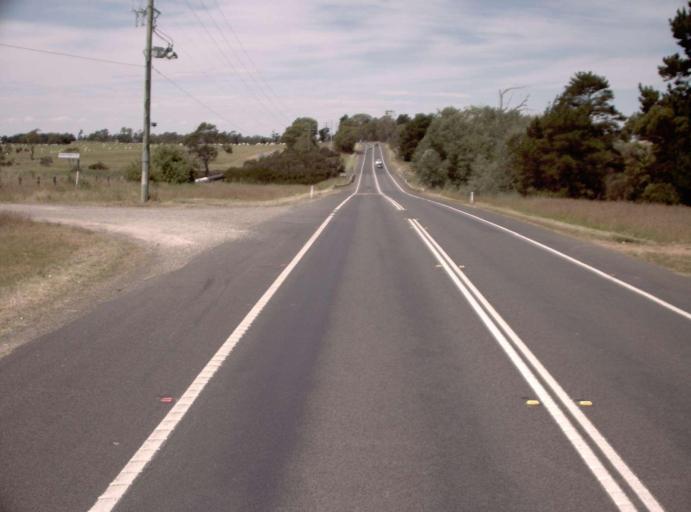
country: AU
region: Victoria
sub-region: Latrobe
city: Traralgon
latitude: -38.1815
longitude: 146.6149
